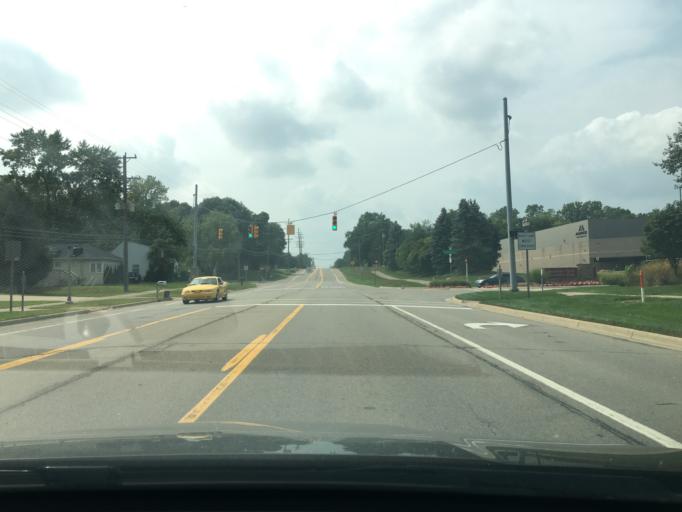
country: US
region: Michigan
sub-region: Oakland County
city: Rochester Hills
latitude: 42.6345
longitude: -83.1927
